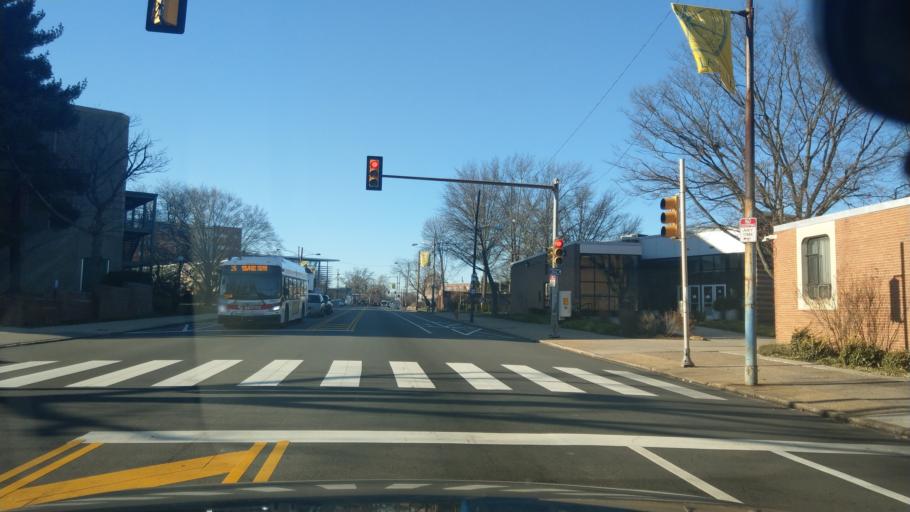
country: US
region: Pennsylvania
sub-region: Montgomery County
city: Wyndmoor
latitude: 40.0401
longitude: -75.1556
